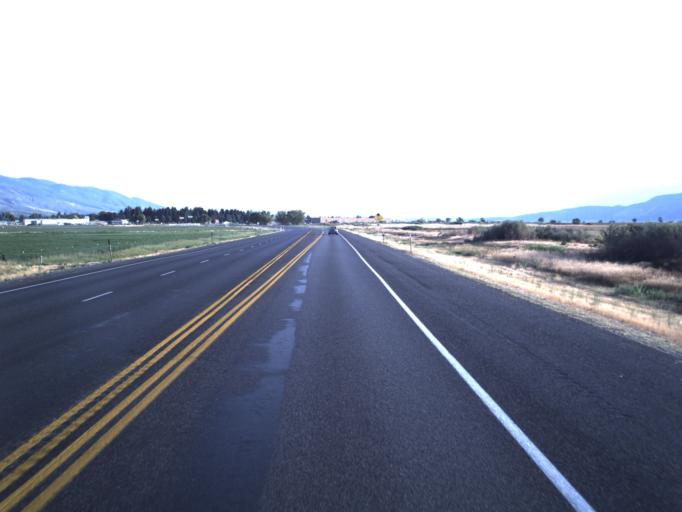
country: US
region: Utah
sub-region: Sanpete County
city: Ephraim
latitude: 39.3830
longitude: -111.5843
